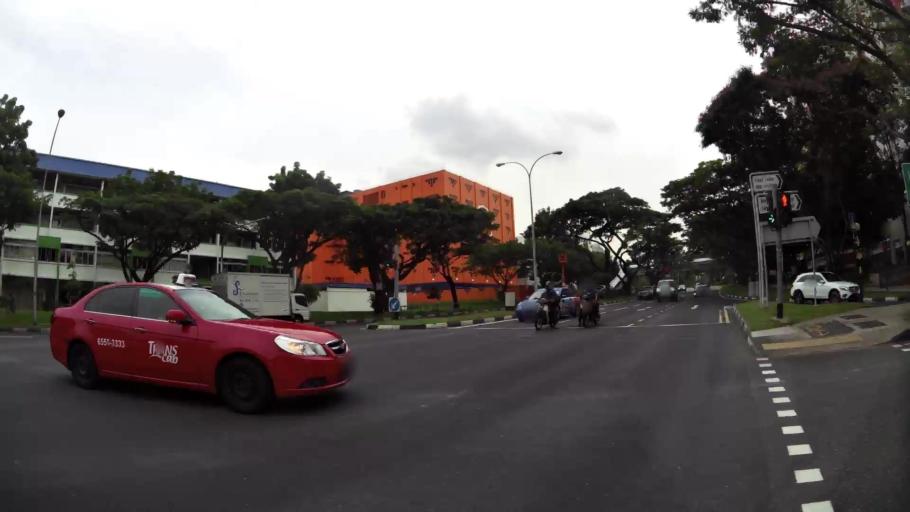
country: SG
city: Singapore
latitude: 1.3522
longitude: 103.8905
